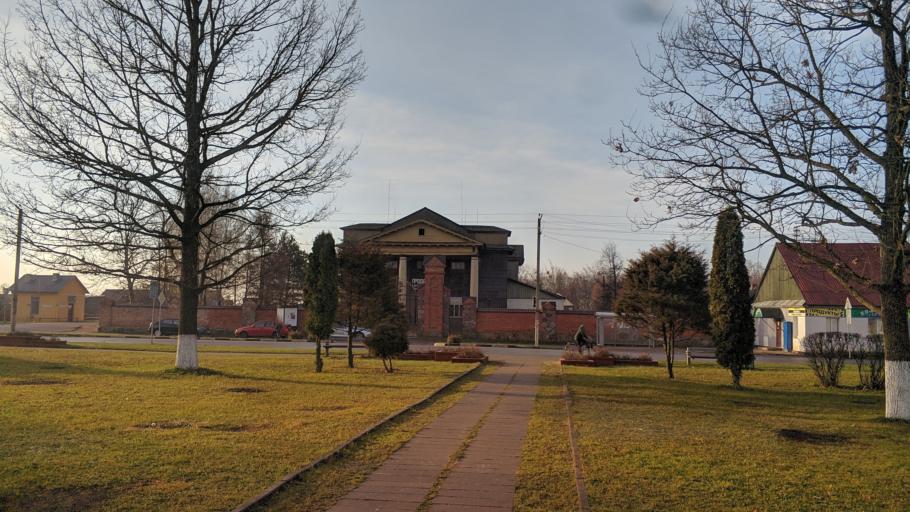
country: BY
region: Minsk
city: Uzda
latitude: 53.4581
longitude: 27.2173
